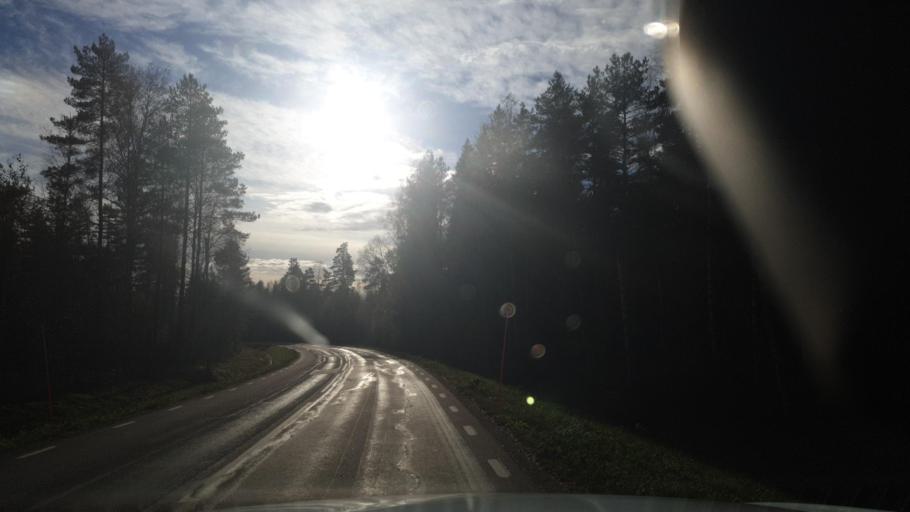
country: SE
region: Vaermland
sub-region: Eda Kommun
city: Charlottenberg
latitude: 59.8940
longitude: 12.2983
